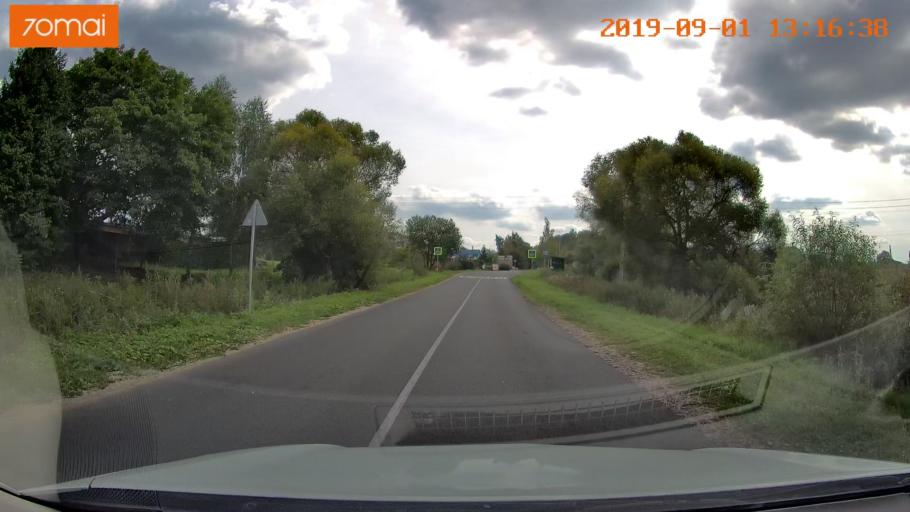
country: RU
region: Kaluga
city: Maloyaroslavets
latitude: 54.9432
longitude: 36.4586
